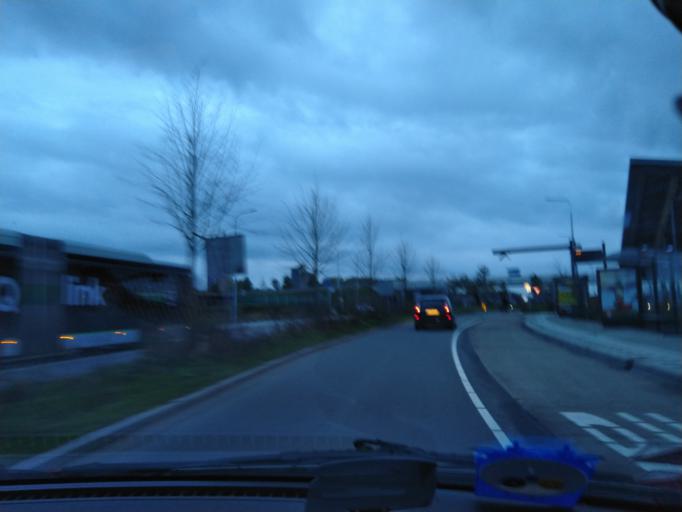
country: NL
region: Groningen
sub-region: Gemeente Groningen
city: Korrewegwijk
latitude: 53.2370
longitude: 6.5205
